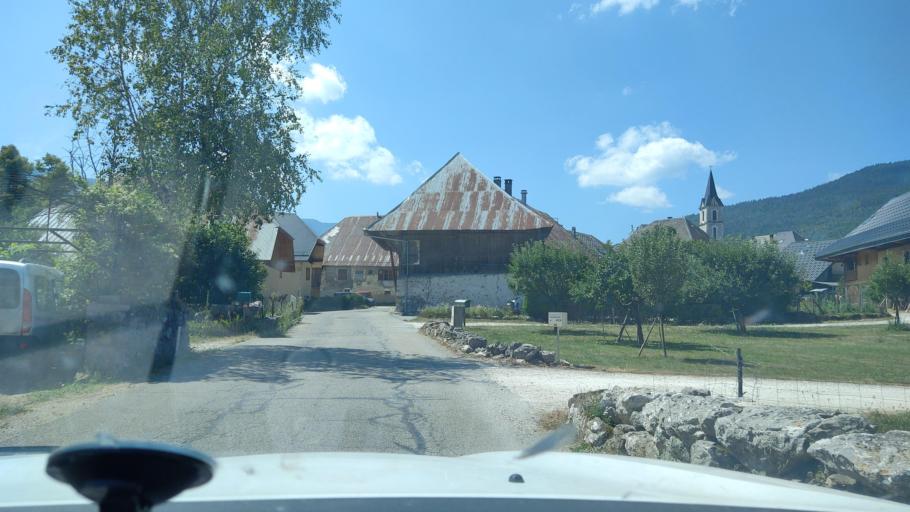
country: FR
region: Rhone-Alpes
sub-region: Departement de la Haute-Savoie
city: Gruffy
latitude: 45.7145
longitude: 6.0873
